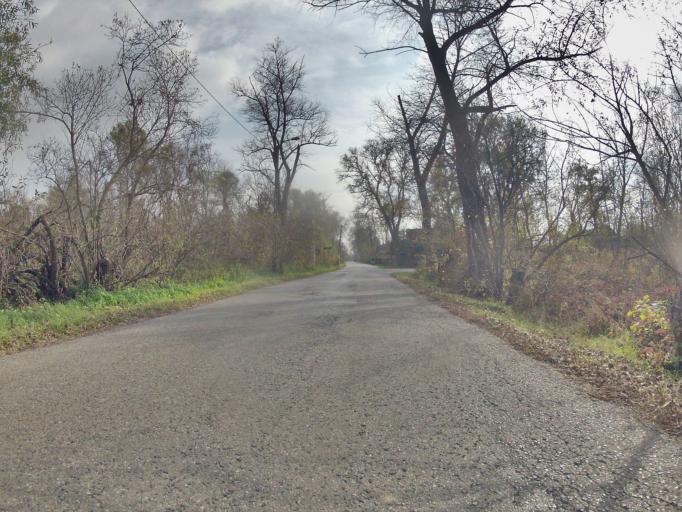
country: PL
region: Lesser Poland Voivodeship
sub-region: Powiat wielicki
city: Wegrzce Wielkie
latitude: 50.0611
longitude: 20.1080
